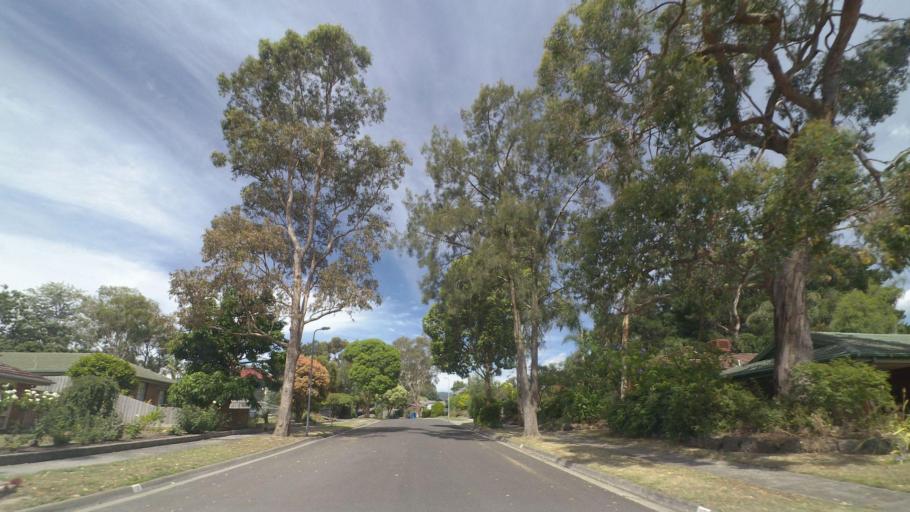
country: AU
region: Victoria
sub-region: Knox
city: The Basin
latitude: -37.8487
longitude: 145.3008
